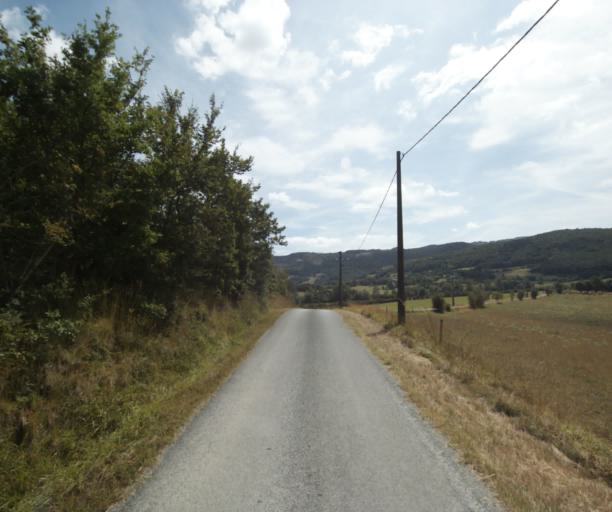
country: FR
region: Midi-Pyrenees
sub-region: Departement du Tarn
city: Dourgne
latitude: 43.4755
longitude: 2.1123
